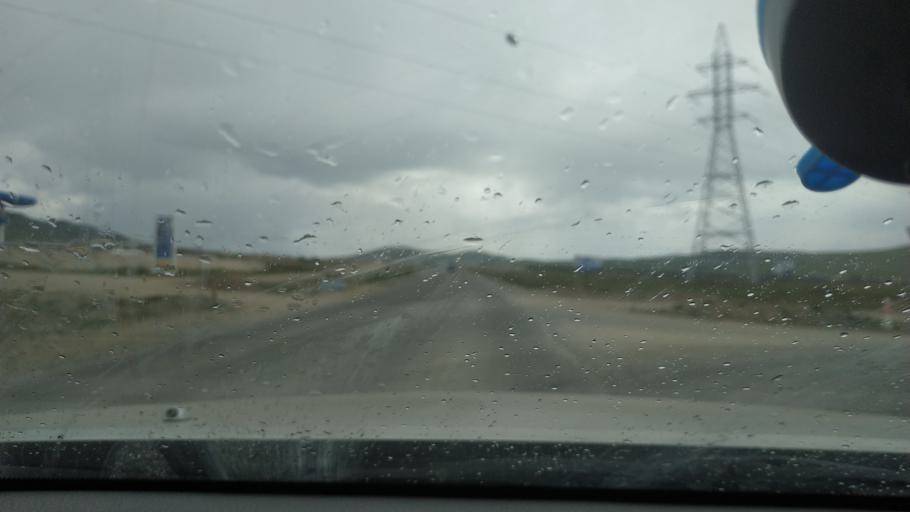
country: MN
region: Ulaanbaatar
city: Ulaanbaatar
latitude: 47.8179
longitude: 106.7577
